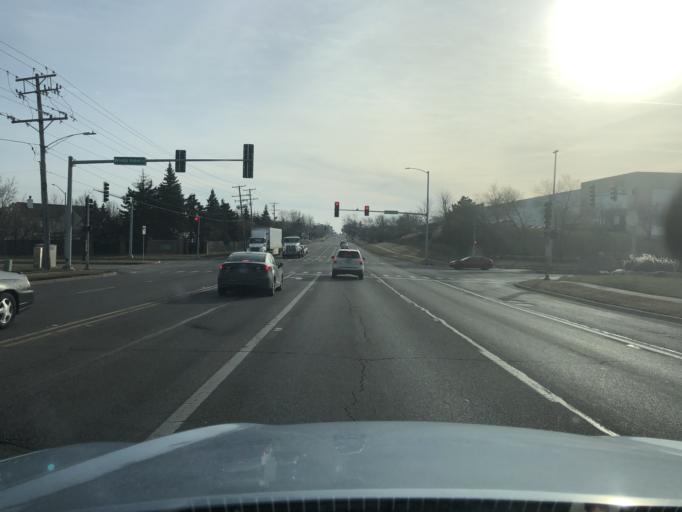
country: US
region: Illinois
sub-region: DuPage County
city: Glendale Heights
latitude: 41.9272
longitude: -88.0810
